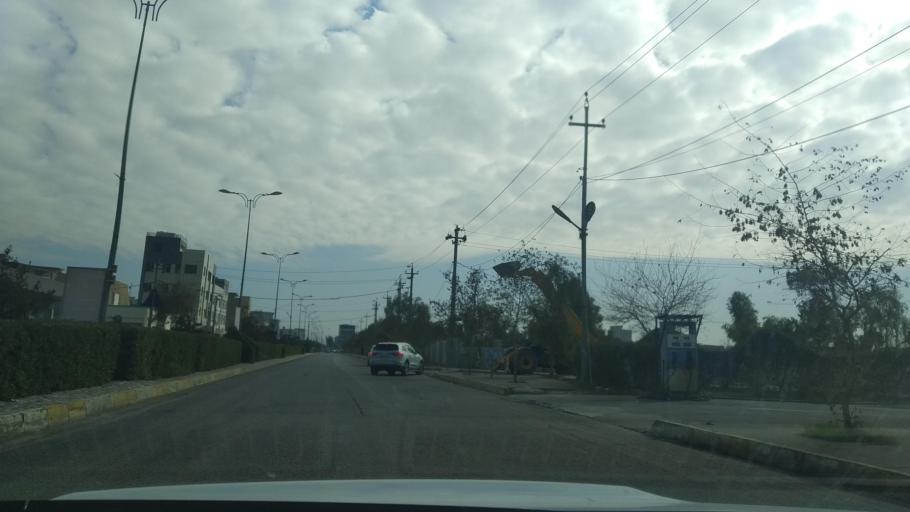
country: IQ
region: Arbil
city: Erbil
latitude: 36.1753
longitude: 44.0329
